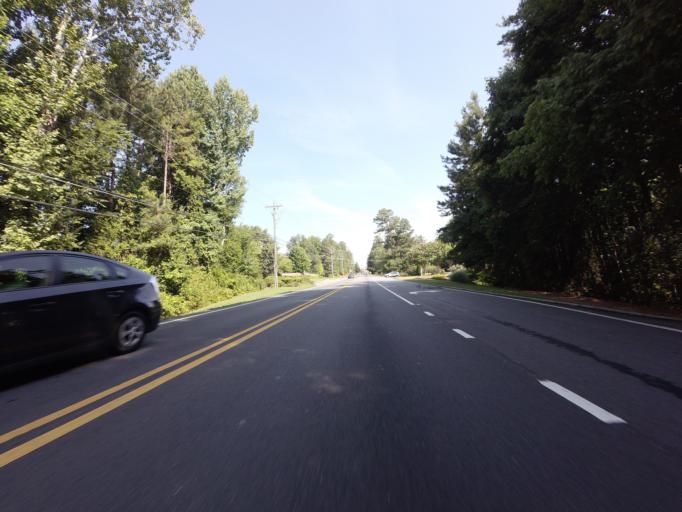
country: US
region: Georgia
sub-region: Fulton County
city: Johns Creek
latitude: 34.0601
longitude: -84.2071
